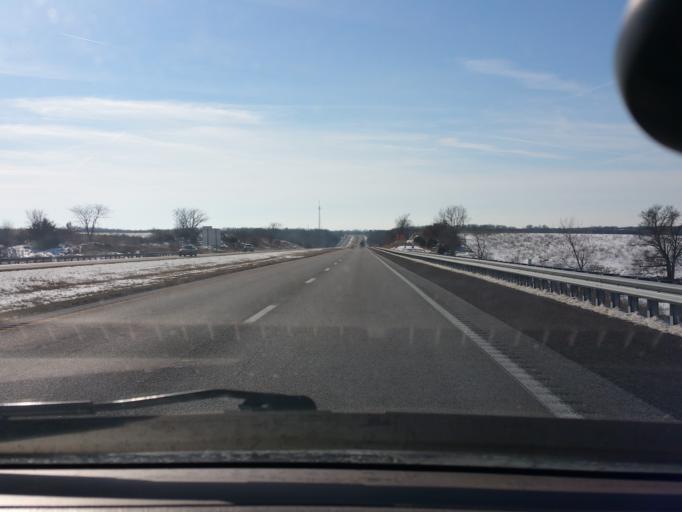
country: US
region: Missouri
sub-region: Clinton County
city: Cameron
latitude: 39.8862
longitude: -94.1593
